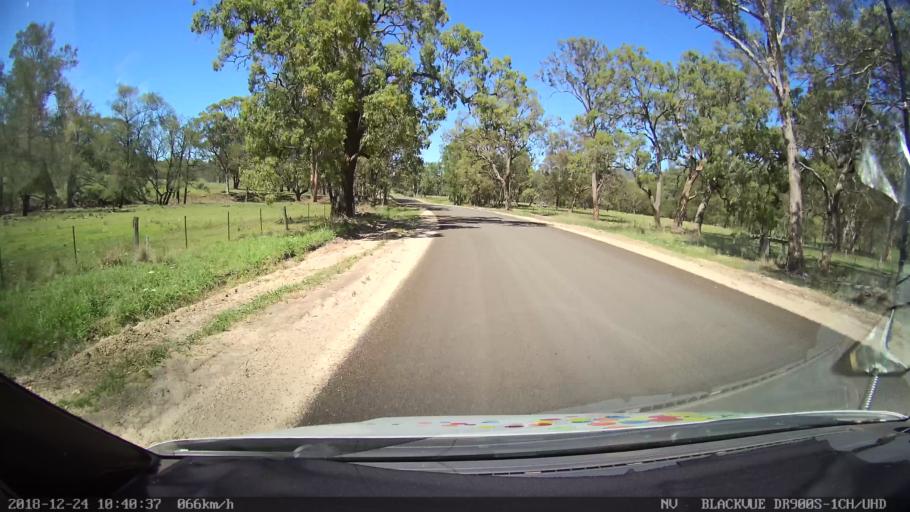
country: AU
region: New South Wales
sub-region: Upper Hunter Shire
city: Merriwa
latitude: -31.8627
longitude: 150.4658
